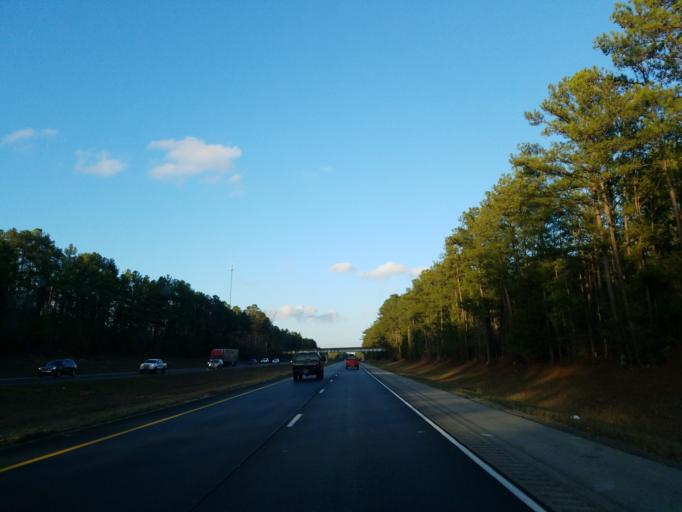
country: US
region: Mississippi
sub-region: Clarke County
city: Stonewall
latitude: 32.2405
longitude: -88.8292
